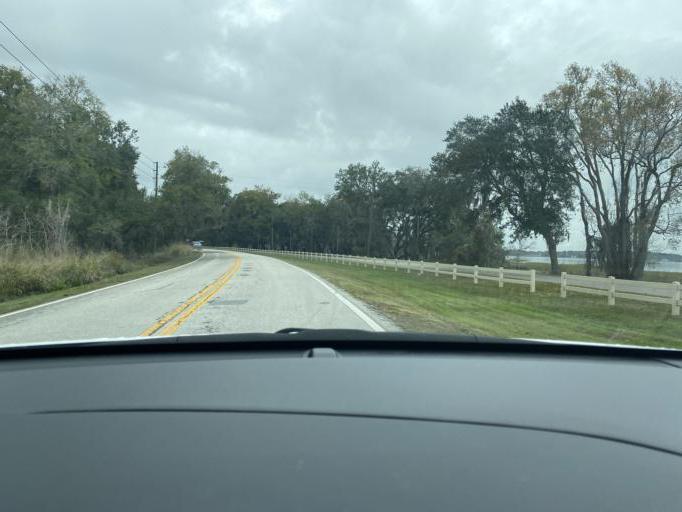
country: US
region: Florida
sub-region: Lake County
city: Clermont
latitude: 28.5676
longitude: -81.7775
